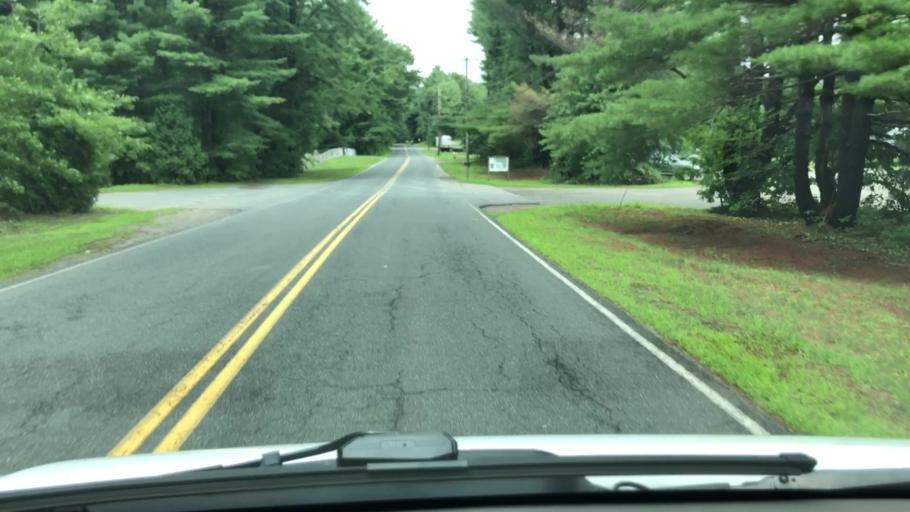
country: US
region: Massachusetts
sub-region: Franklin County
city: South Deerfield
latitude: 42.4631
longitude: -72.6090
